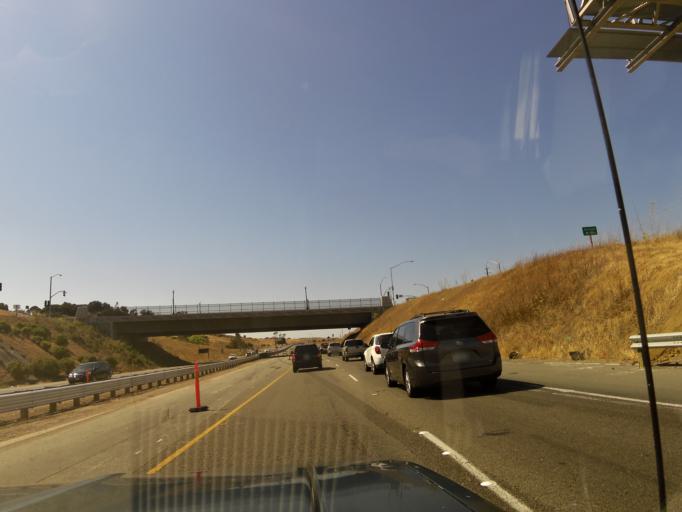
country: US
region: California
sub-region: Sonoma County
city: Petaluma
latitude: 38.2204
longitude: -122.6063
